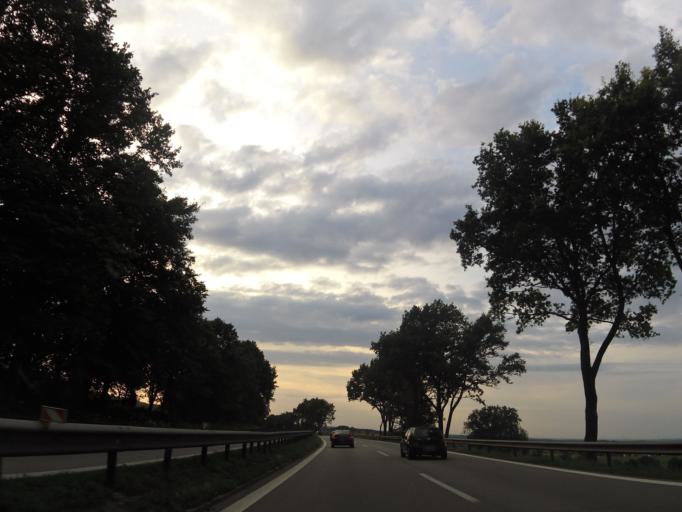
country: DE
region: Bavaria
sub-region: Upper Bavaria
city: Teisendorf
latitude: 47.8243
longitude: 12.8224
